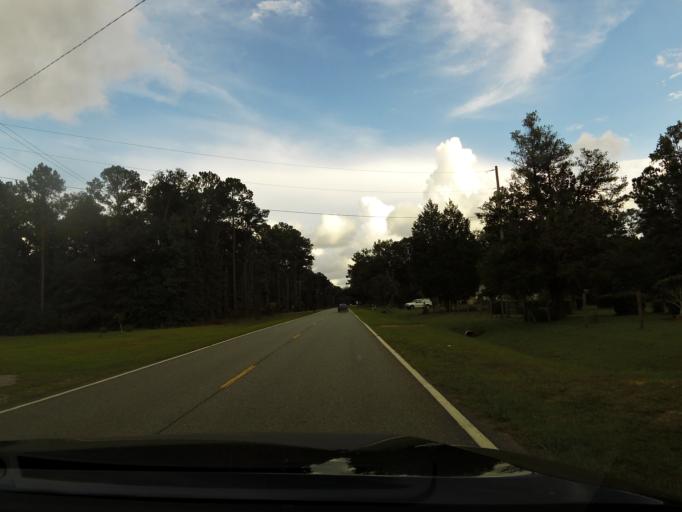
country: US
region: Georgia
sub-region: Liberty County
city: Midway
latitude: 31.8485
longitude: -81.4195
